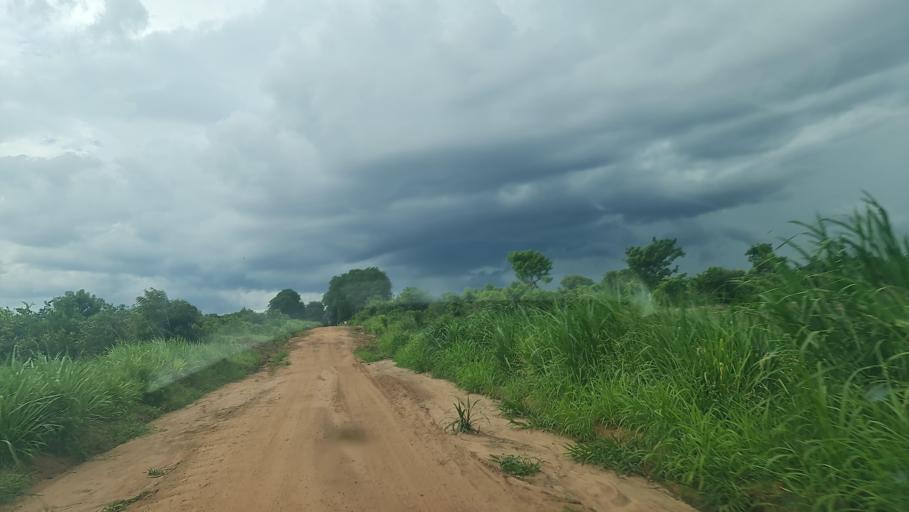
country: MW
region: Southern Region
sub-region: Nsanje District
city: Nsanje
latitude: -17.3810
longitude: 35.5815
